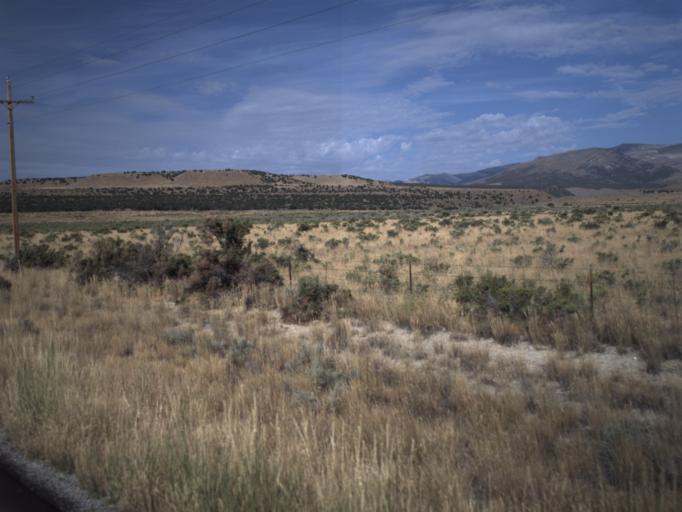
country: US
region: Idaho
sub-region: Minidoka County
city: Heyburn
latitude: 41.8229
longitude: -113.1862
